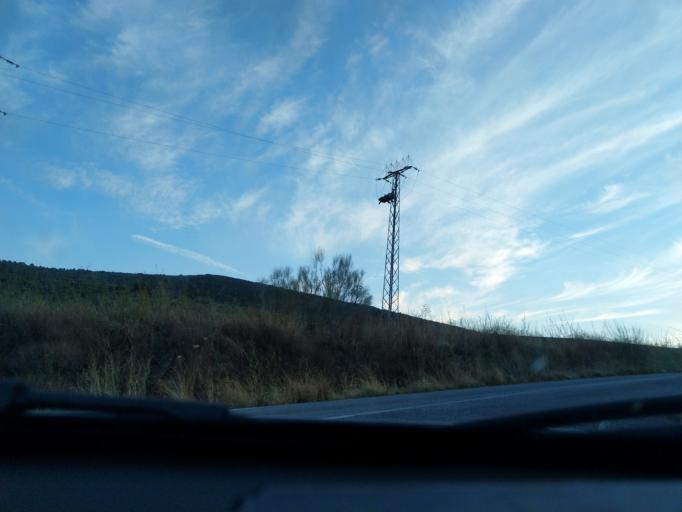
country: ES
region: Extremadura
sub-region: Provincia de Badajoz
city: Reina
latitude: 38.1530
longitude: -5.9024
